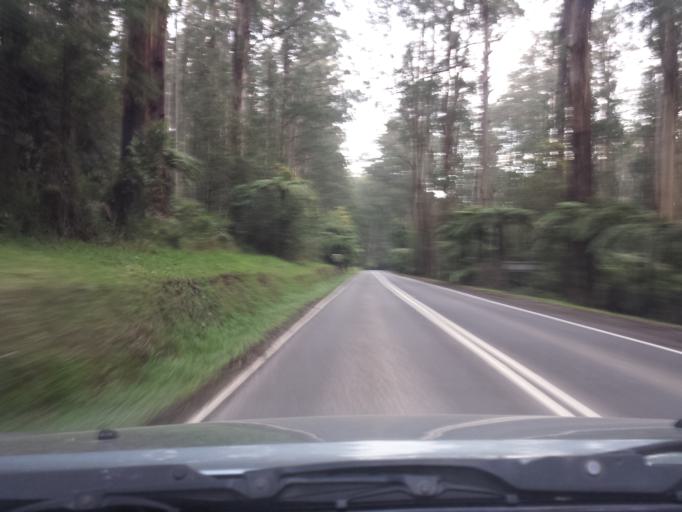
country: AU
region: Victoria
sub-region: Yarra Ranges
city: Kallista
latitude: -37.8887
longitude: 145.3689
